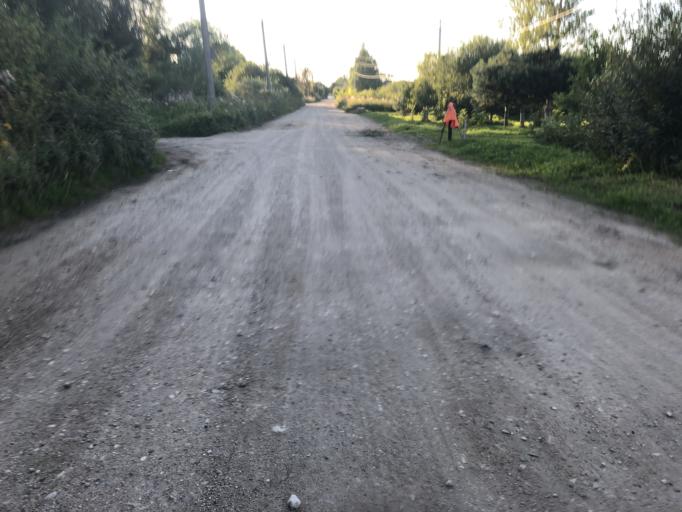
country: RU
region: Tverskaya
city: Rzhev
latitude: 56.2434
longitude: 34.3080
